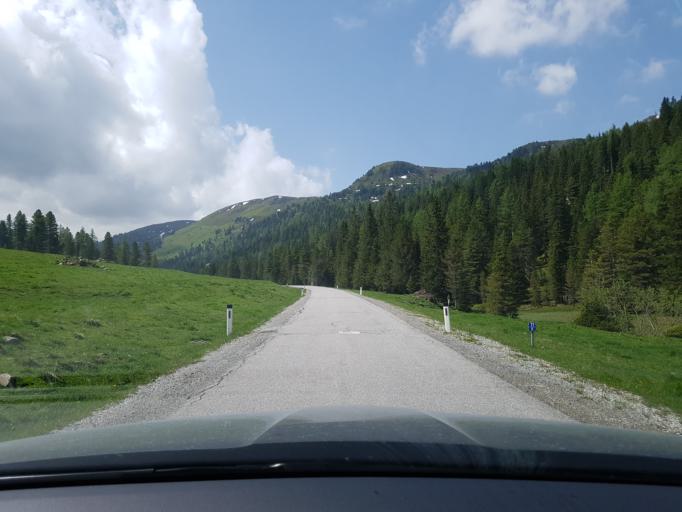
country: AT
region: Salzburg
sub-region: Politischer Bezirk Tamsweg
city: Thomatal
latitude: 47.0058
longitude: 13.7655
